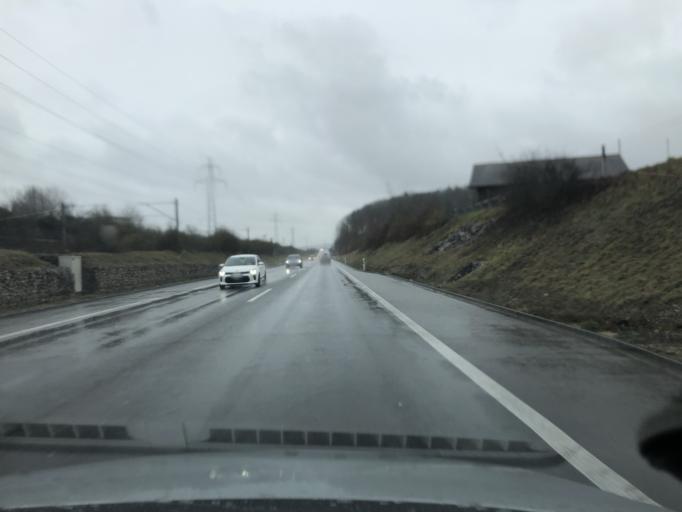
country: CH
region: Aargau
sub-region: Bezirk Brugg
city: Hausen
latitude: 47.4589
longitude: 8.2095
